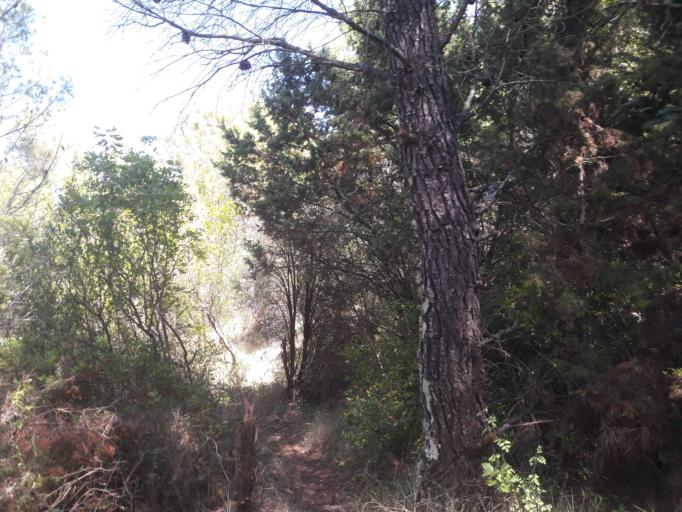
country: HR
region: Sibensko-Kniniska
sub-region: Grad Sibenik
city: Sibenik
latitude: 43.6914
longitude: 15.8576
